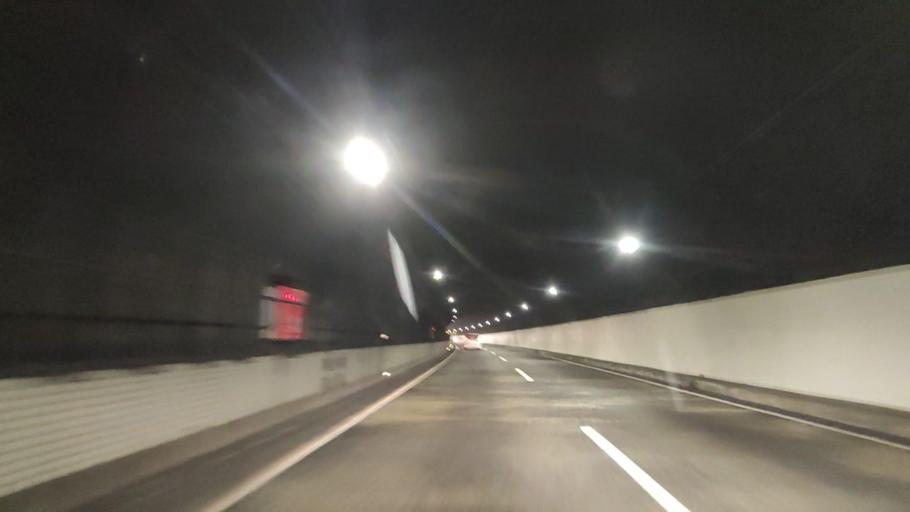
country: JP
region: Okayama
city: Okayama-shi
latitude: 34.6824
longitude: 133.8489
